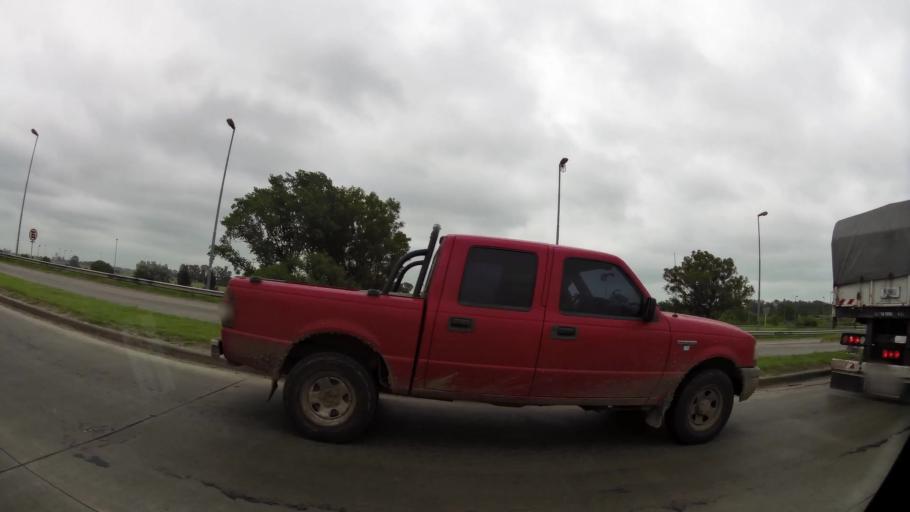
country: AR
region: Buenos Aires
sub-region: Partido de La Plata
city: La Plata
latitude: -35.0345
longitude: -58.0913
